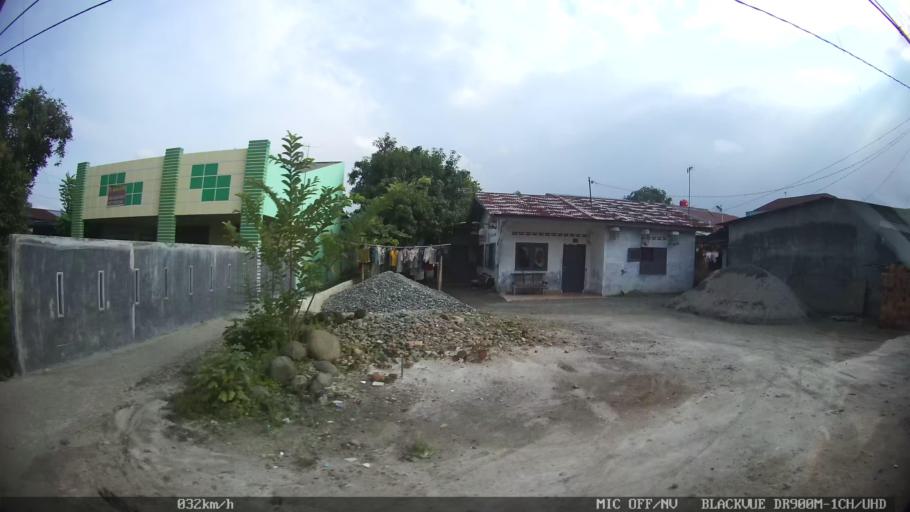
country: ID
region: North Sumatra
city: Medan
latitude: 3.6054
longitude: 98.7398
